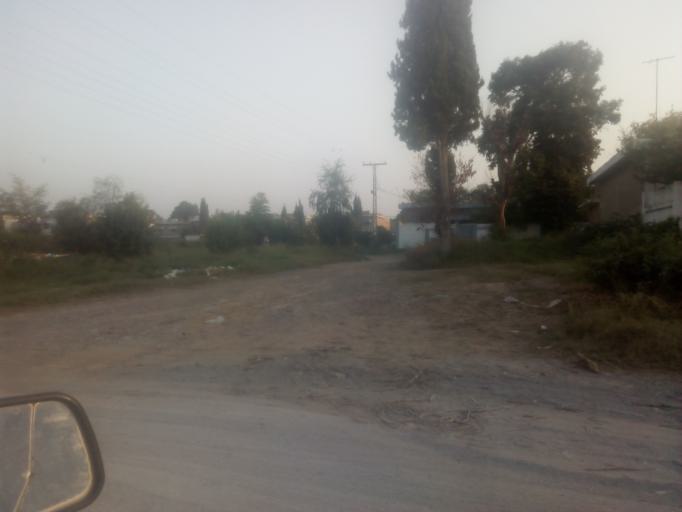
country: PK
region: Islamabad
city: Islamabad
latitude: 33.7734
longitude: 72.8137
